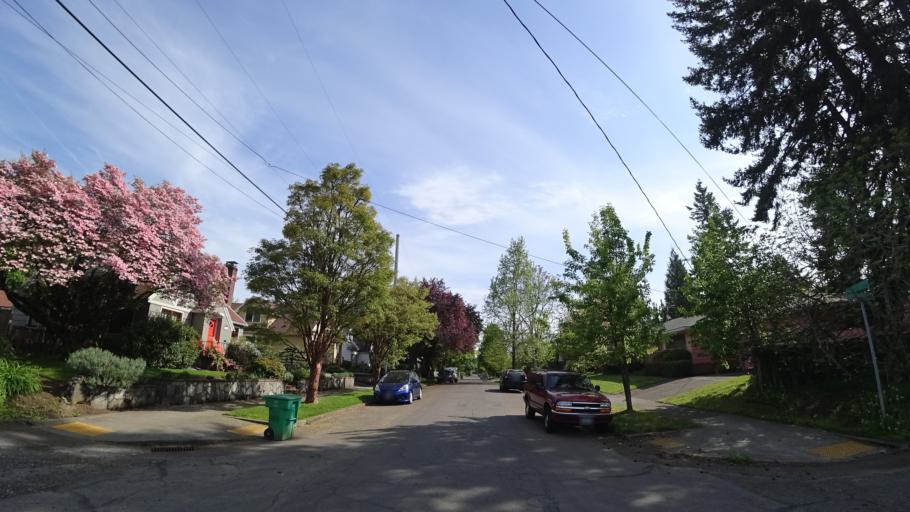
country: US
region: Oregon
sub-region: Clackamas County
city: Milwaukie
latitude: 45.4778
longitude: -122.6217
